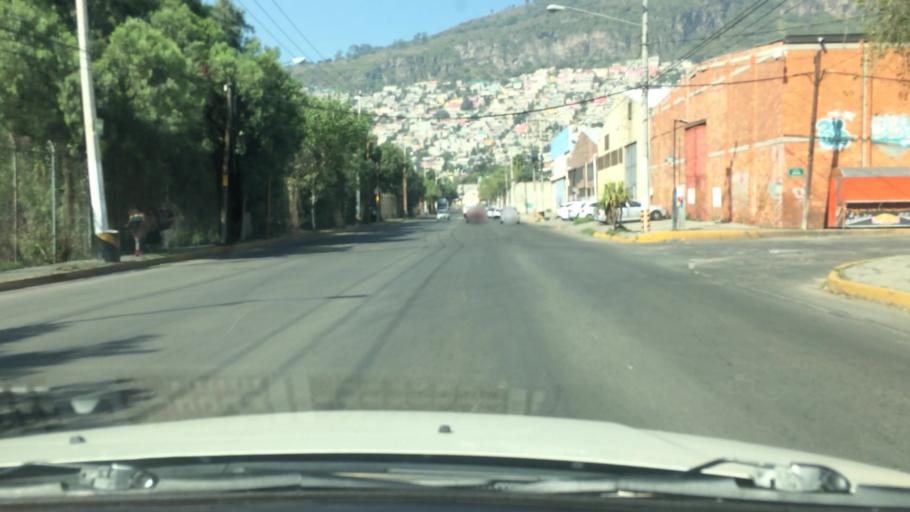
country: MX
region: Mexico
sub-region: Tlalnepantla de Baz
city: Puerto Escondido (Tepeolulco Puerto Escondido)
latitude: 19.5270
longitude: -99.1165
